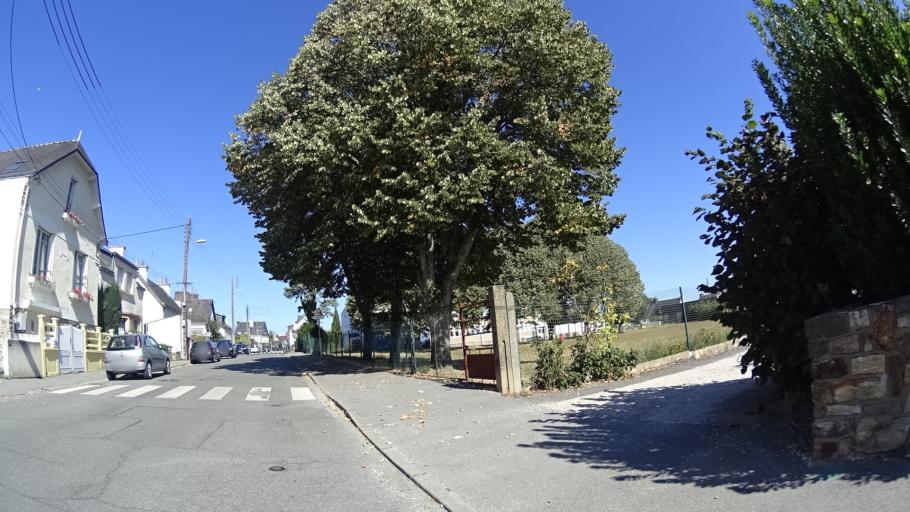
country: FR
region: Brittany
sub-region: Departement du Morbihan
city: Vannes
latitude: 47.6427
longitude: -2.7652
